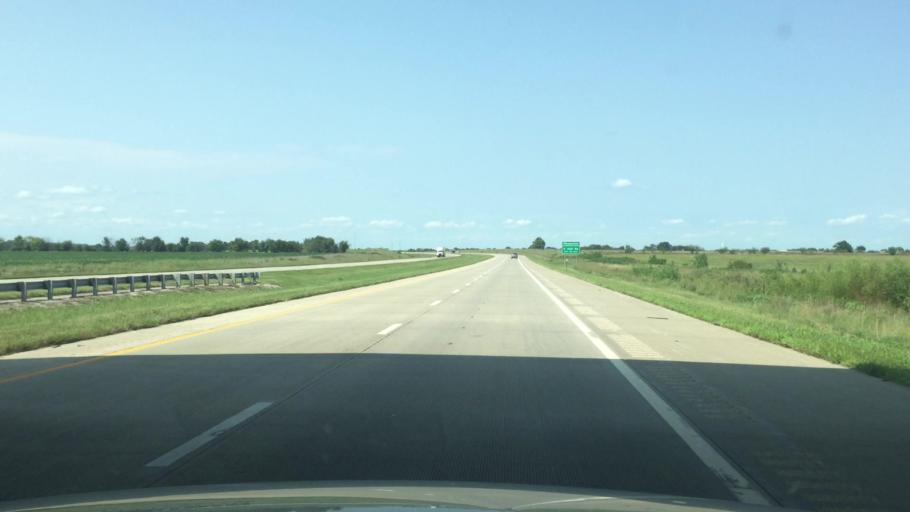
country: US
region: Kansas
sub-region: Linn County
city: Pleasanton
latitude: 38.1680
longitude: -94.6957
